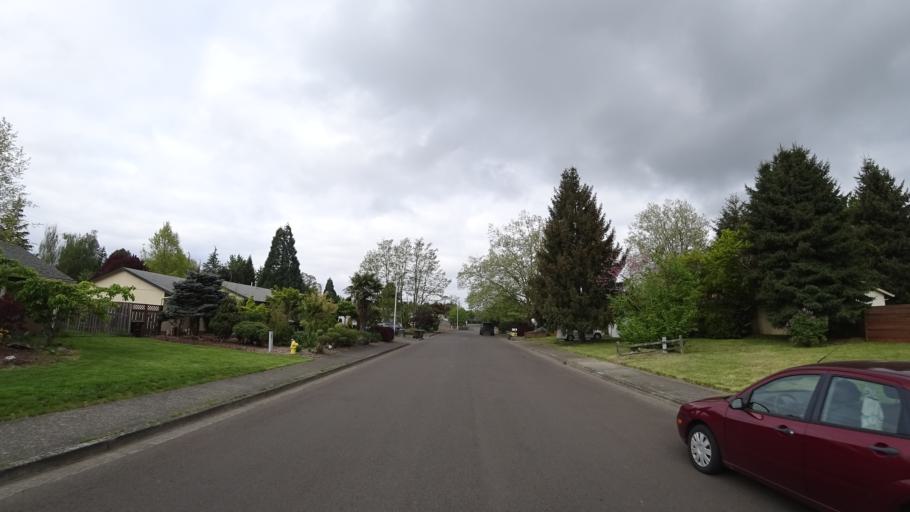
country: US
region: Oregon
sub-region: Washington County
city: Hillsboro
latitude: 45.5381
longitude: -122.9767
